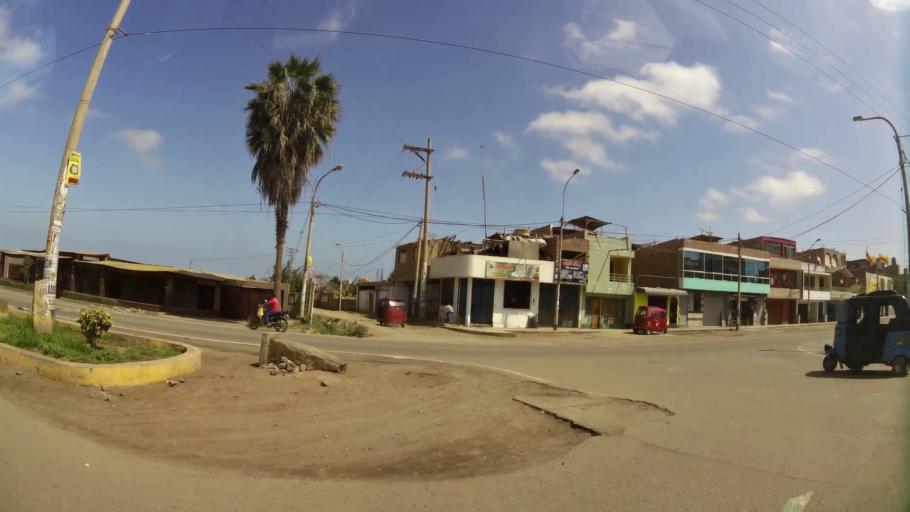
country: PE
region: Lima
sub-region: Provincia de Canete
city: Mala
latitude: -12.6614
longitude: -76.6327
